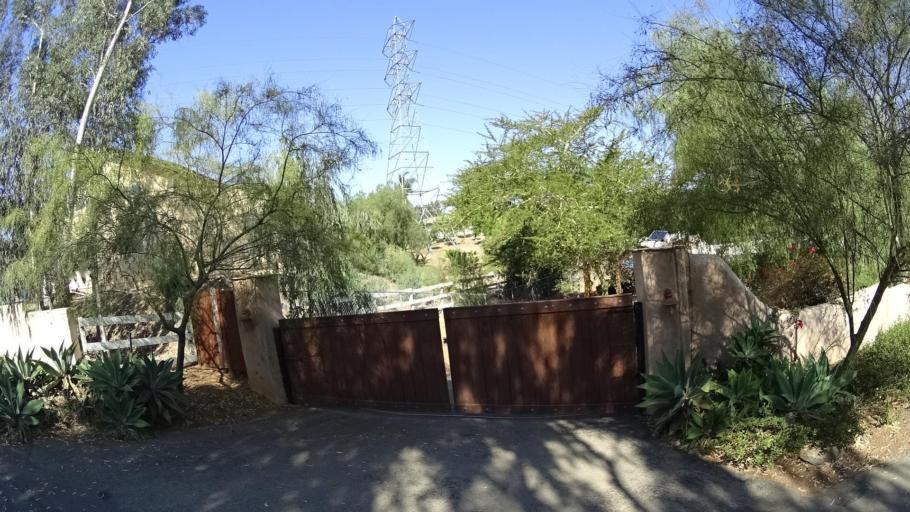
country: US
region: California
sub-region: San Diego County
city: Rancho Santa Fe
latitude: 33.0288
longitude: -117.1684
